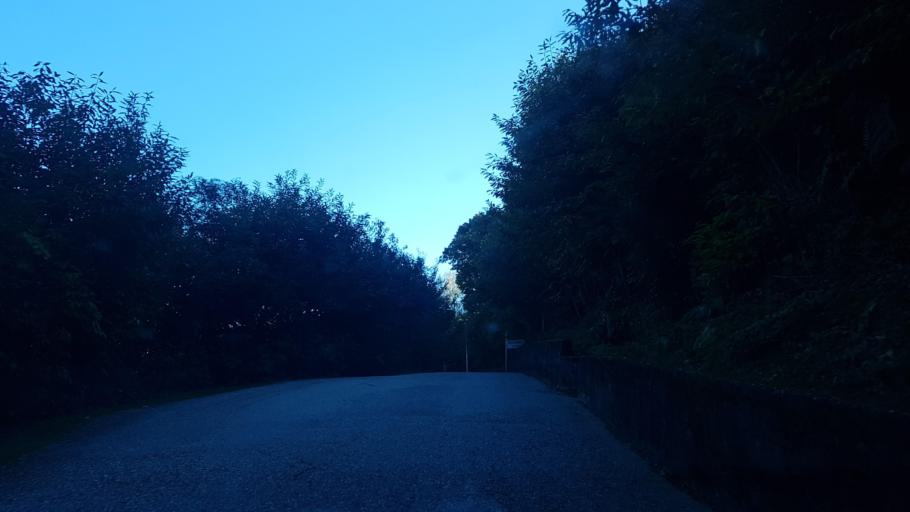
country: IT
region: Piedmont
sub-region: Provincia Verbano-Cusio-Ossola
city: Mergozzo
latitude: 45.9464
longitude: 8.4662
